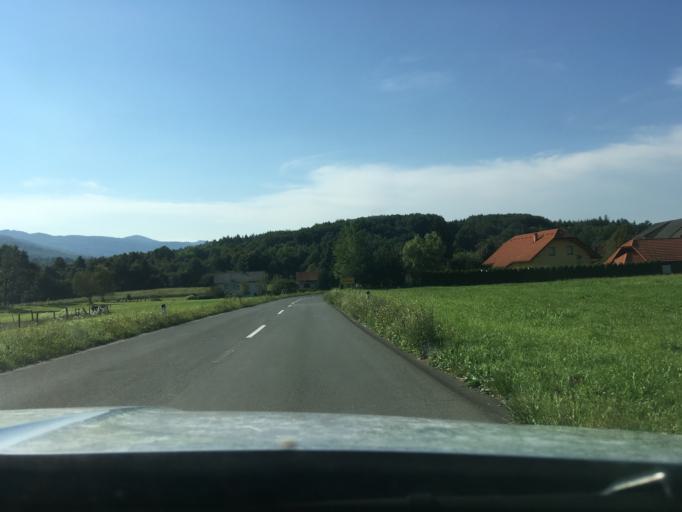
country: SI
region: Crnomelj
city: Crnomelj
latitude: 45.4928
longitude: 15.1914
